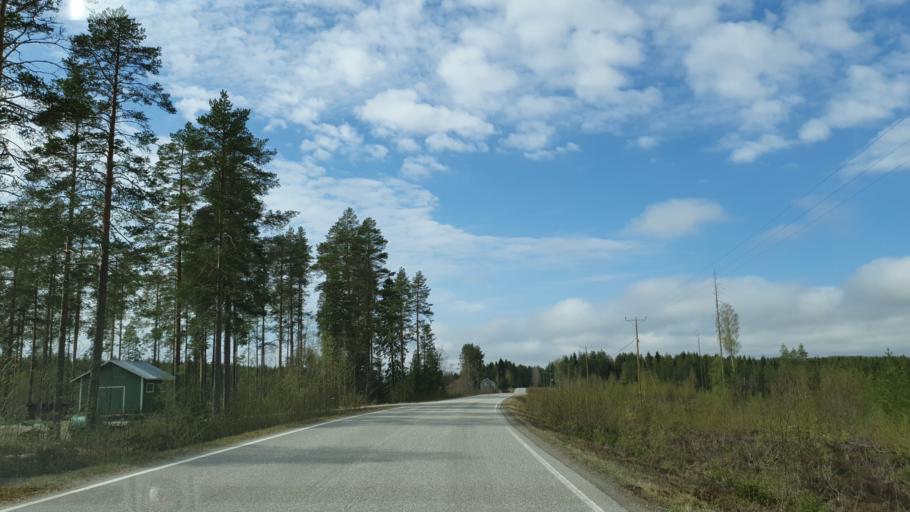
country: FI
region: Kainuu
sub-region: Kehys-Kainuu
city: Kuhmo
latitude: 64.1216
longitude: 29.6680
